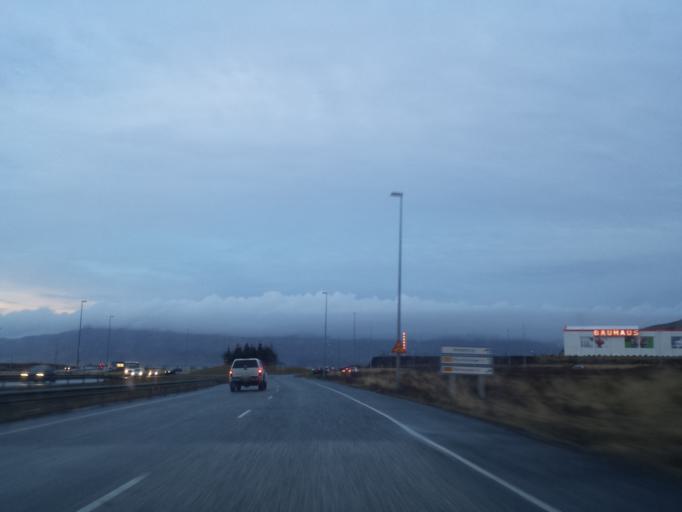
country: IS
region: Capital Region
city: Mosfellsbaer
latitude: 64.1377
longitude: -21.7589
